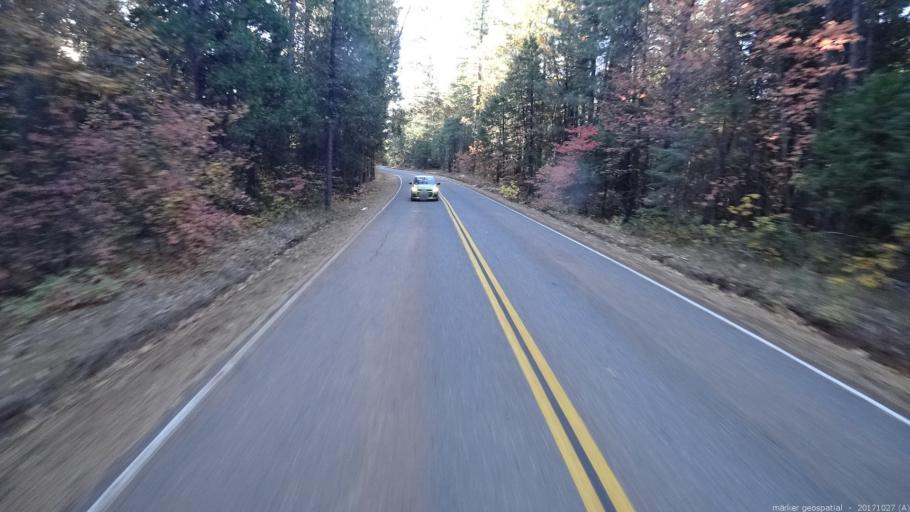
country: US
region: California
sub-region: Shasta County
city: Burney
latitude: 40.9732
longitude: -121.9305
